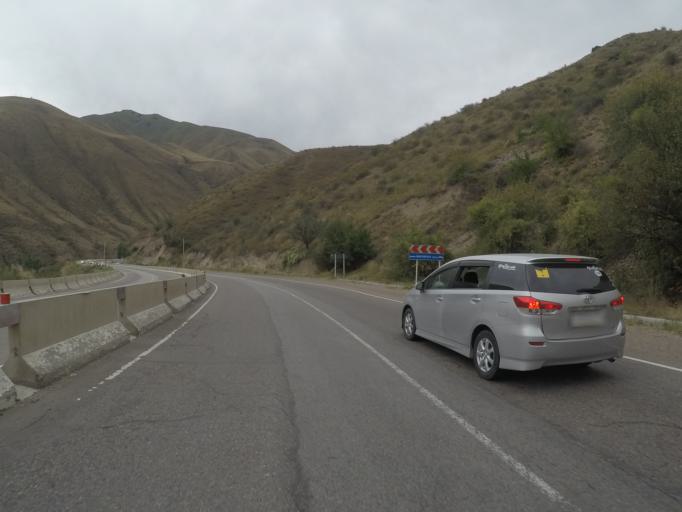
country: KG
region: Chuy
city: Bystrovka
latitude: 42.6615
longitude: 75.8851
